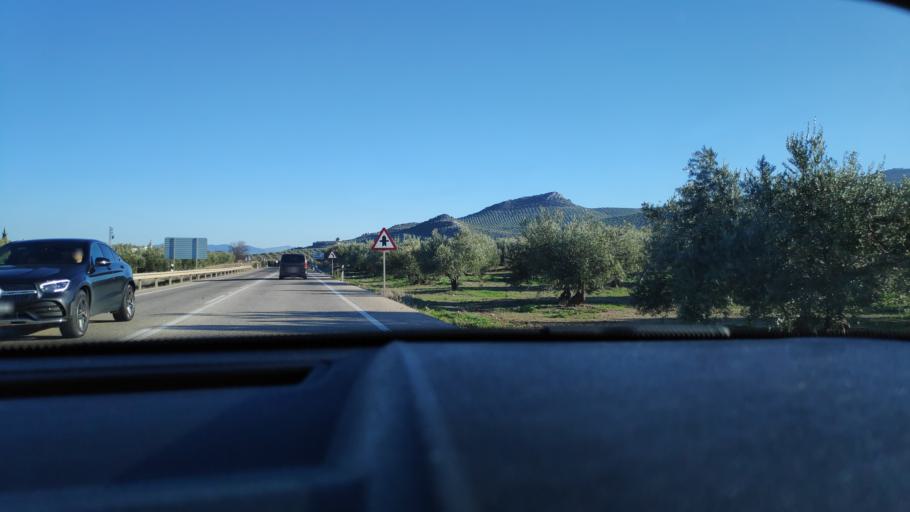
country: ES
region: Andalusia
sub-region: Province of Cordoba
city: Luque
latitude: 37.5657
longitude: -4.2273
